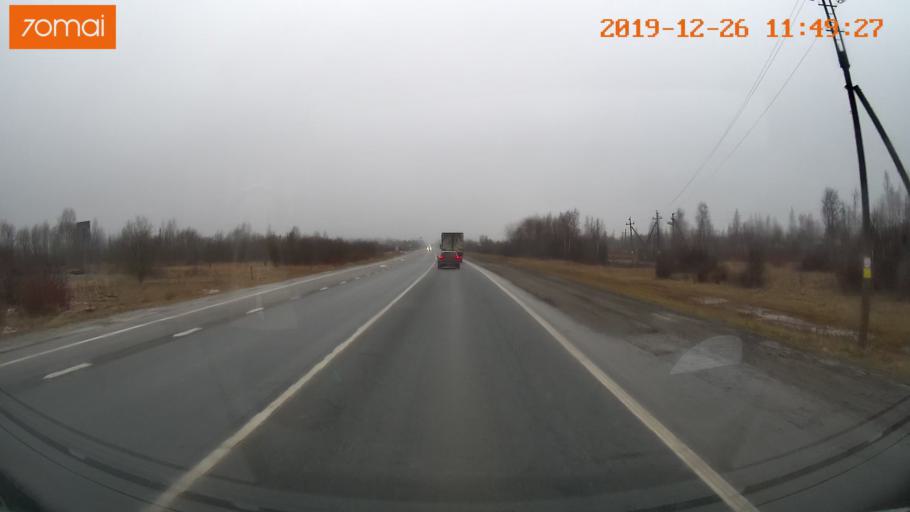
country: RU
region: Vologda
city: Sheksna
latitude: 59.2486
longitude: 38.4194
